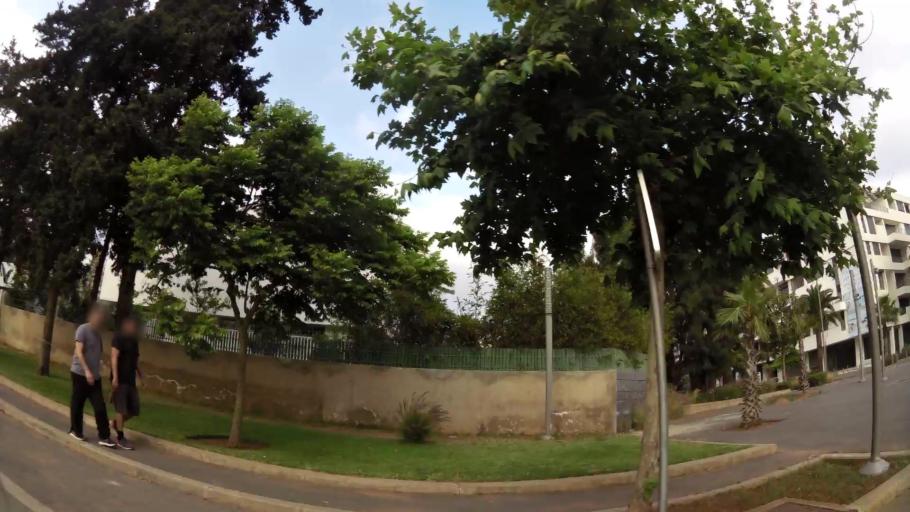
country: MA
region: Rabat-Sale-Zemmour-Zaer
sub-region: Rabat
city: Rabat
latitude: 33.9512
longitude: -6.8383
